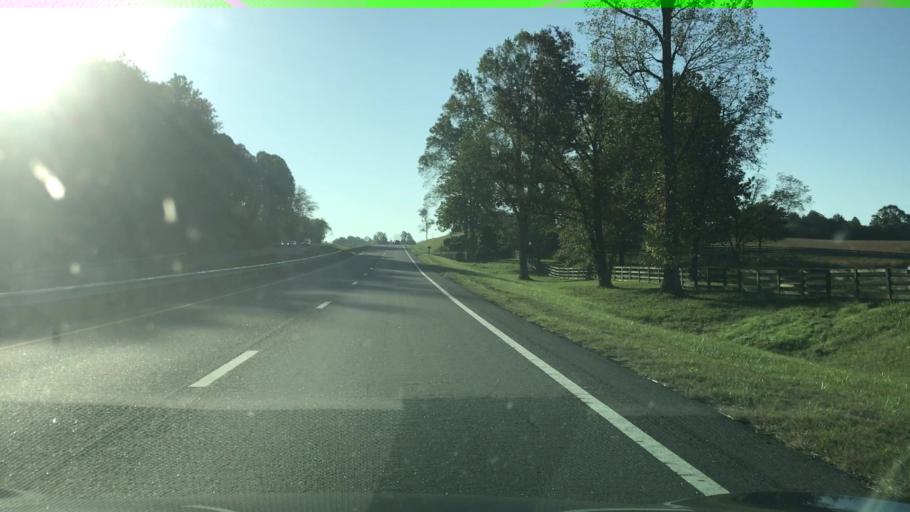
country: US
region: Virginia
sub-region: Bedford County
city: Forest
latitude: 37.3054
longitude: -79.3892
